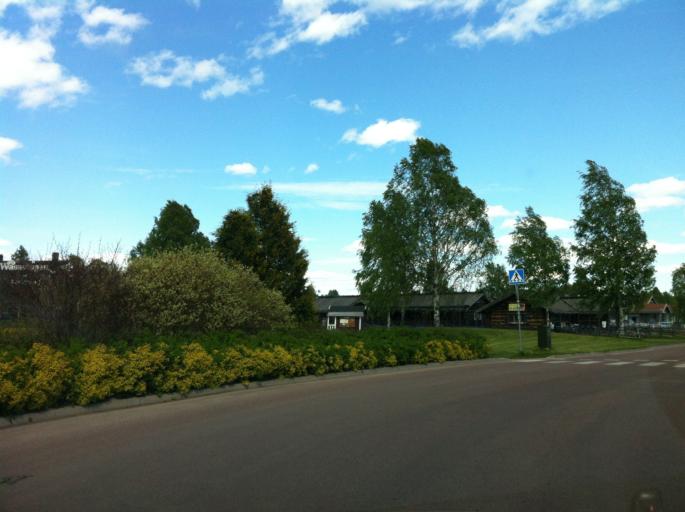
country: SE
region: Dalarna
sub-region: Mora Kommun
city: Mora
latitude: 61.0067
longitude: 14.5467
